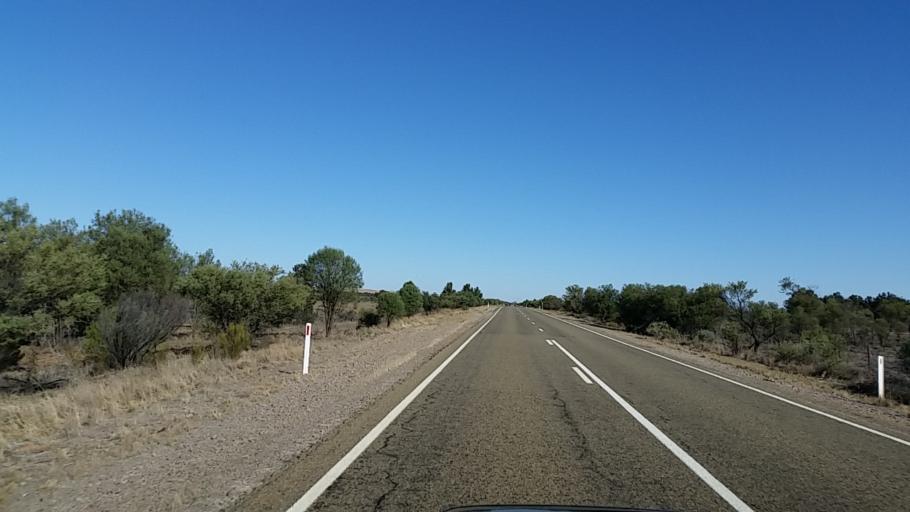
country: AU
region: South Australia
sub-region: Flinders Ranges
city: Quorn
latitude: -32.5123
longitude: 138.5471
